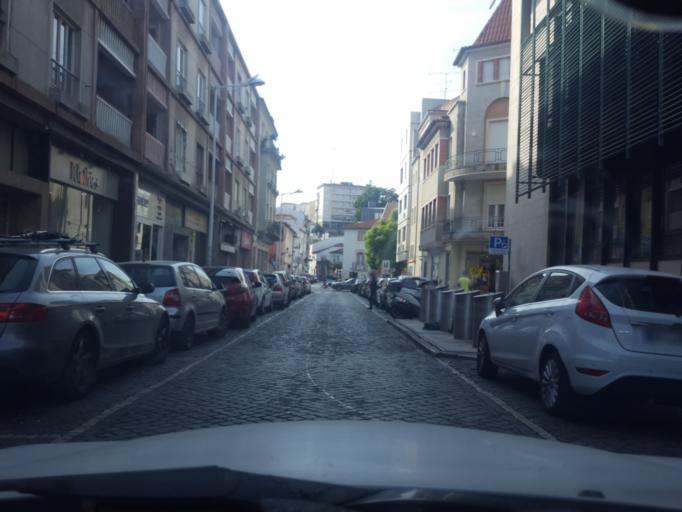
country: PT
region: Leiria
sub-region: Leiria
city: Leiria
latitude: 39.7436
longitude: -8.8075
